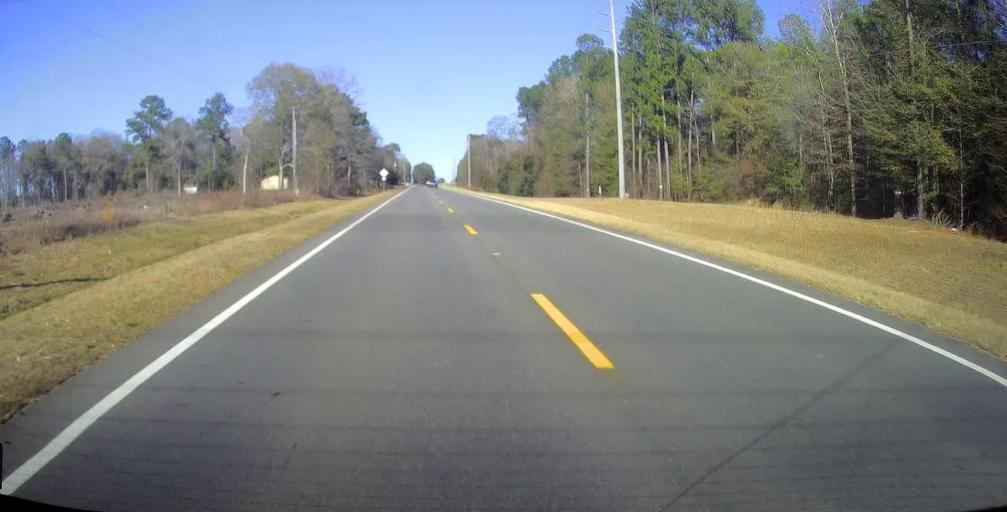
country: US
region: Georgia
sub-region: Macon County
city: Oglethorpe
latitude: 32.2302
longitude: -84.0979
